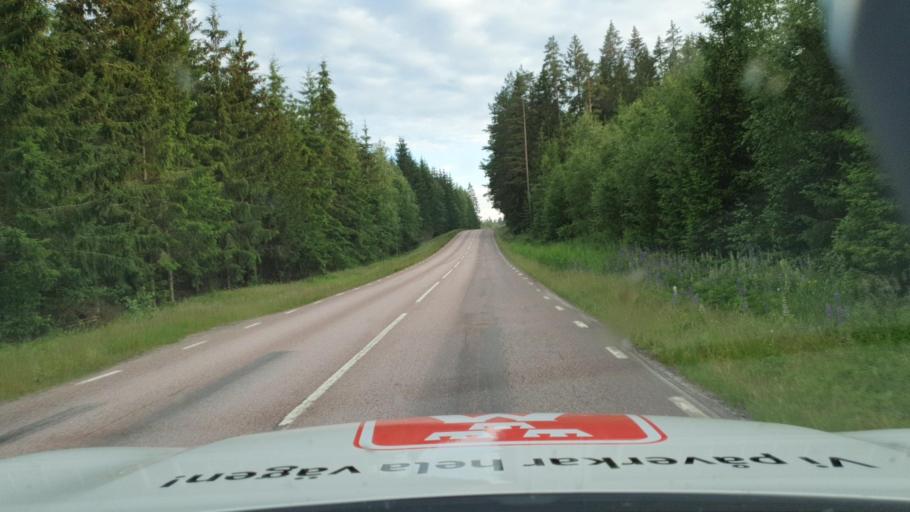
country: SE
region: Vaermland
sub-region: Karlstads Kommun
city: Molkom
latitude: 59.5451
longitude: 13.7812
